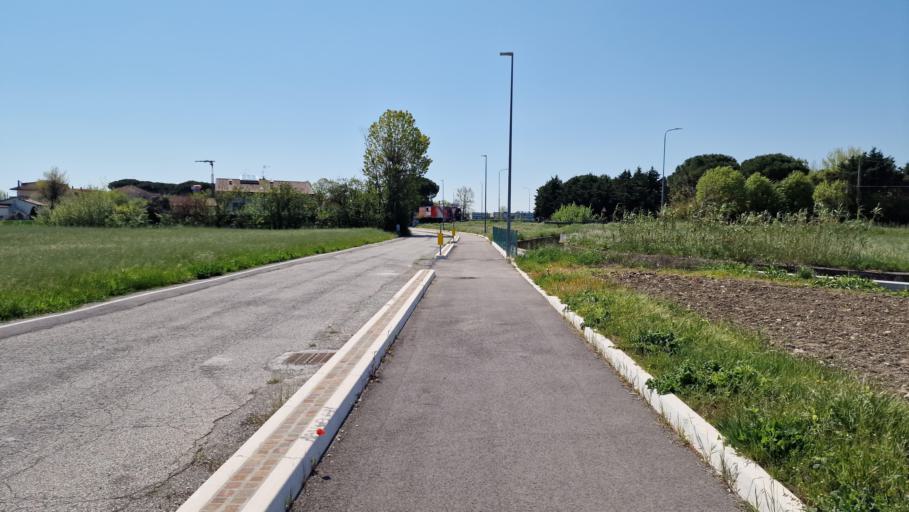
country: IT
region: Emilia-Romagna
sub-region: Provincia di Rimini
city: Bellaria-Igea Marina
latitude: 44.1399
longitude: 12.4650
